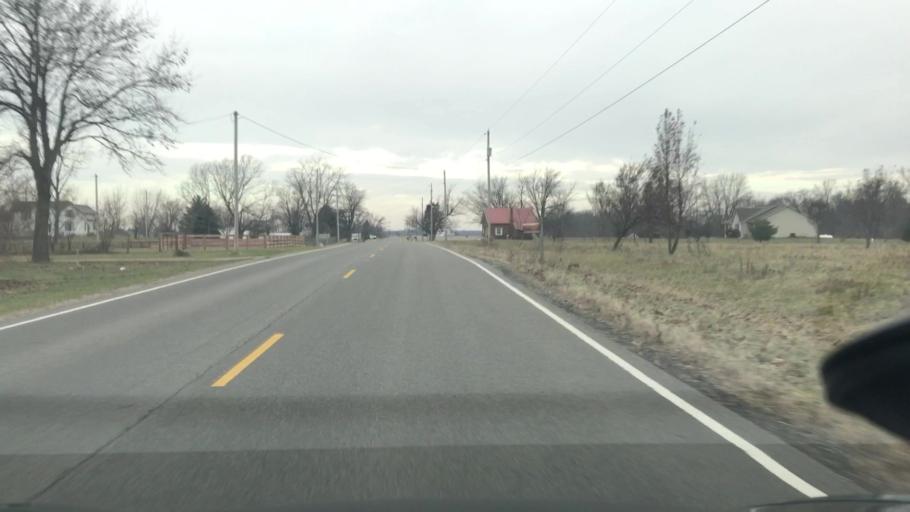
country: US
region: Ohio
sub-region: Madison County
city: London
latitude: 39.8346
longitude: -83.3751
